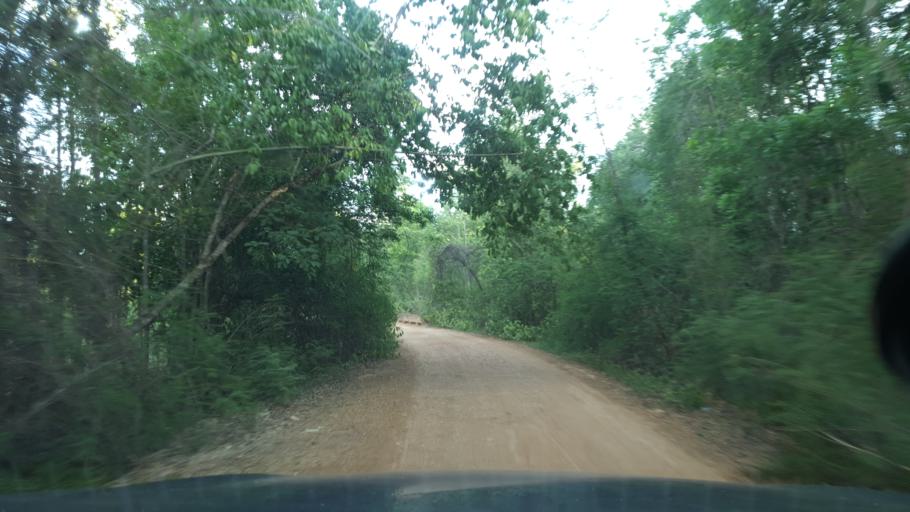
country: TH
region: Lampang
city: Sop Prap
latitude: 17.9538
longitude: 99.3484
